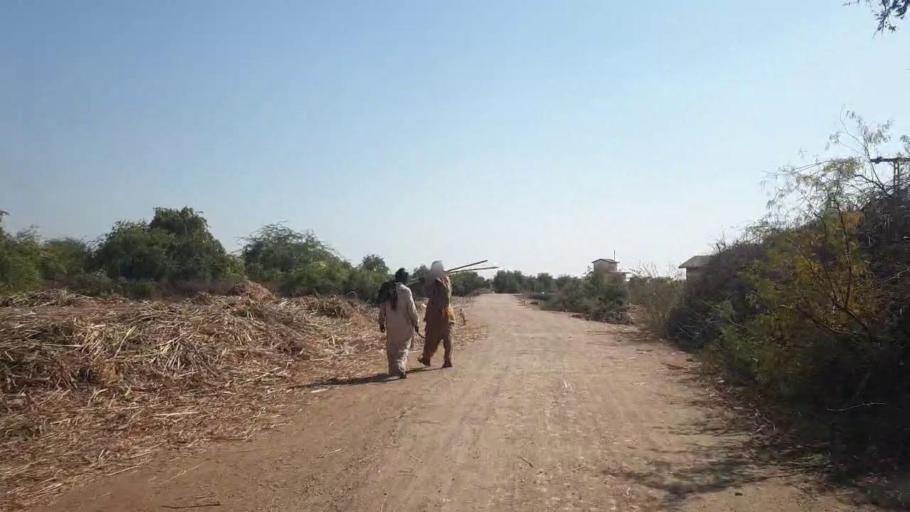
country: PK
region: Sindh
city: Chambar
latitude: 25.3120
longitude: 68.7199
